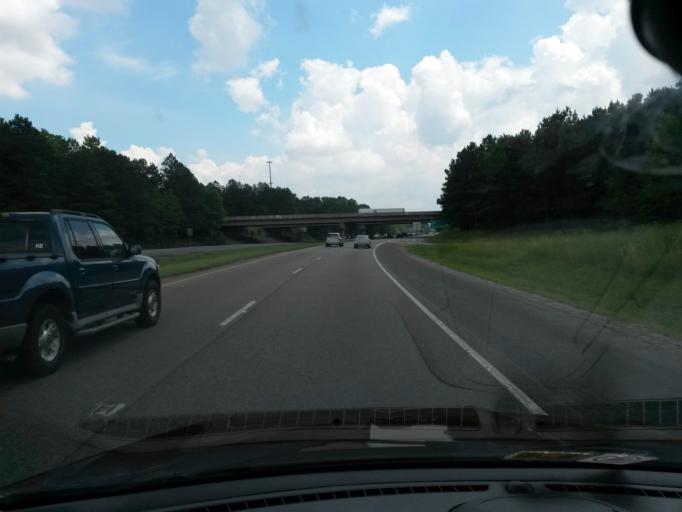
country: US
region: Virginia
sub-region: Chesterfield County
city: Enon
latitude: 37.3442
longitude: -77.3369
